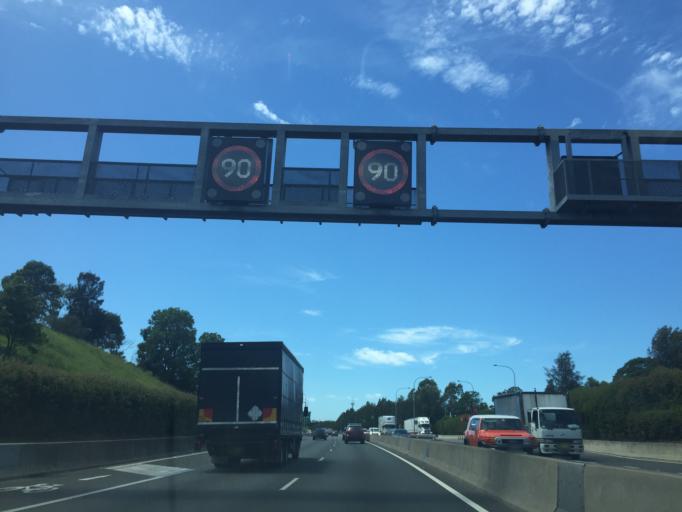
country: AU
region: New South Wales
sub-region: Canterbury
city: Clemton Park
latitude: -33.9404
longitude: 151.0909
